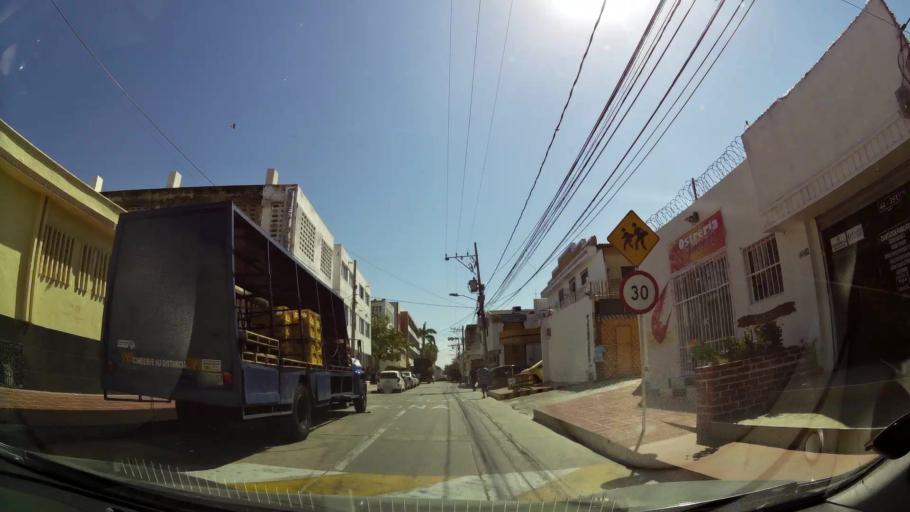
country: CO
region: Atlantico
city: Barranquilla
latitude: 10.9858
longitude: -74.7843
